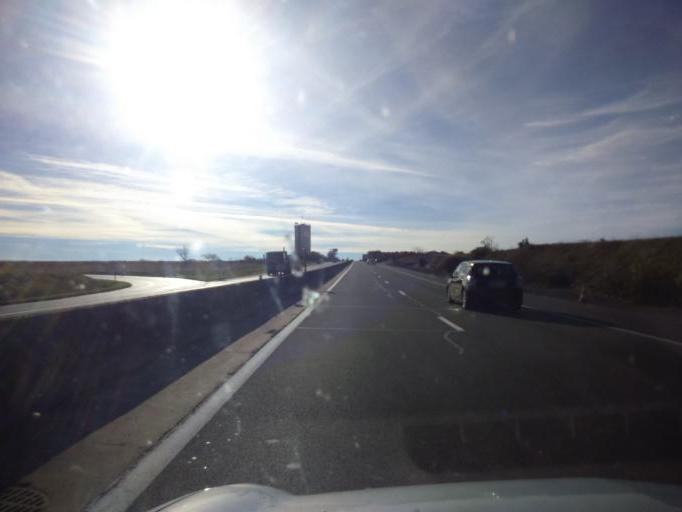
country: FR
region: Poitou-Charentes
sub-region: Departement de la Charente-Maritime
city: Aytre
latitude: 46.1422
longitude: -1.1068
